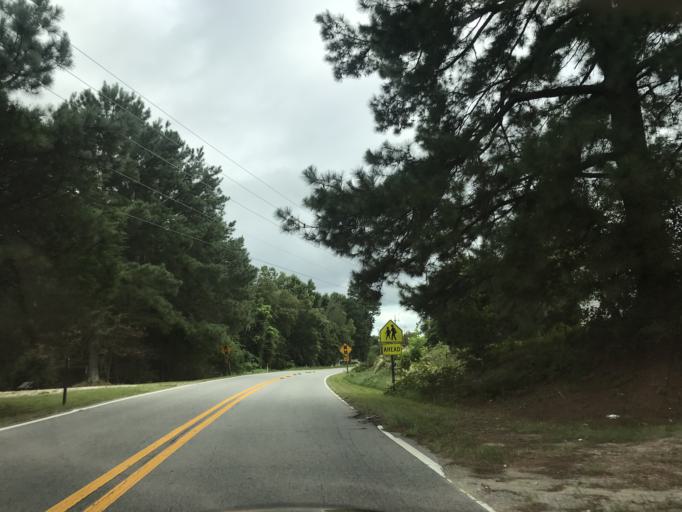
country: US
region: North Carolina
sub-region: Johnston County
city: Clayton
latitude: 35.5829
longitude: -78.5416
